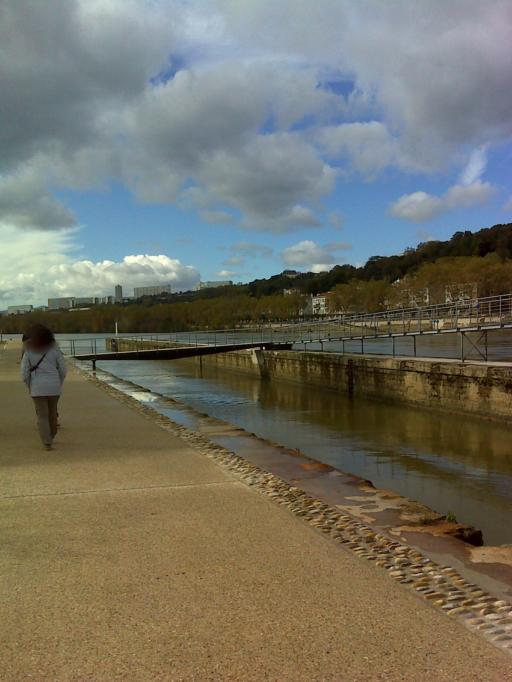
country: FR
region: Rhone-Alpes
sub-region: Departement du Rhone
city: Caluire-et-Cuire
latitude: 45.7957
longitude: 4.8298
